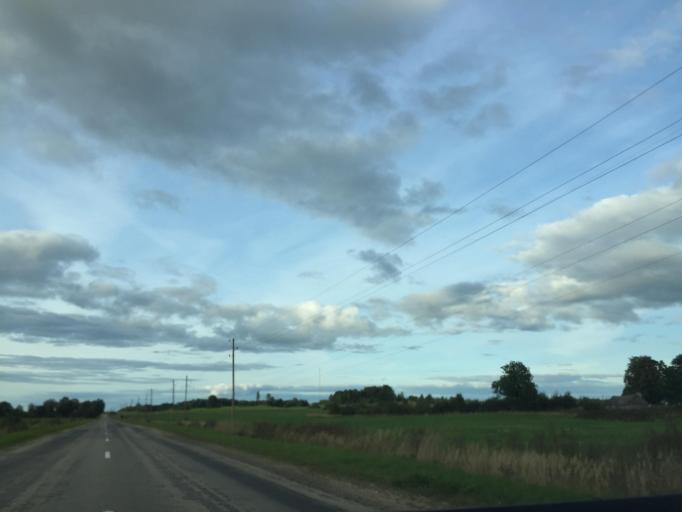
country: LV
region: Nereta
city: Nereta
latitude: 56.2198
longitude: 25.3175
